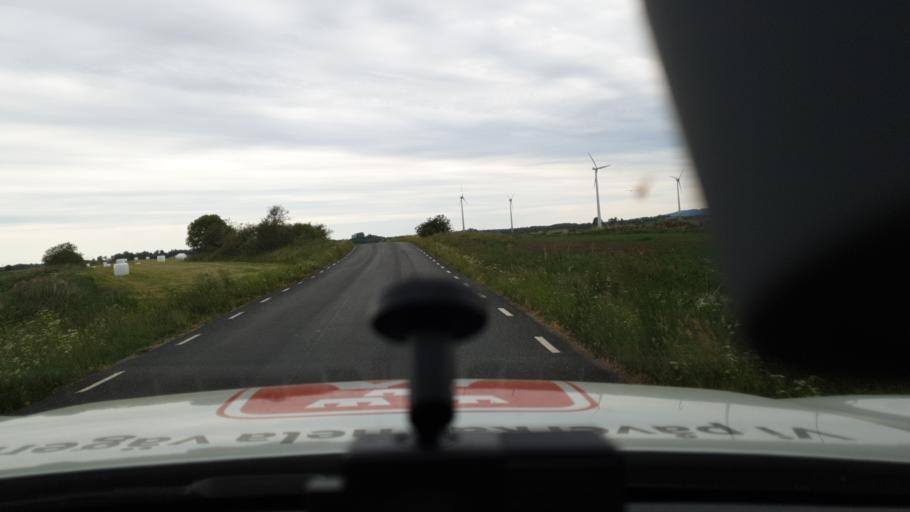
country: SE
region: Vaestra Goetaland
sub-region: Falkopings Kommun
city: Falkoeping
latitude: 58.0918
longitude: 13.5126
